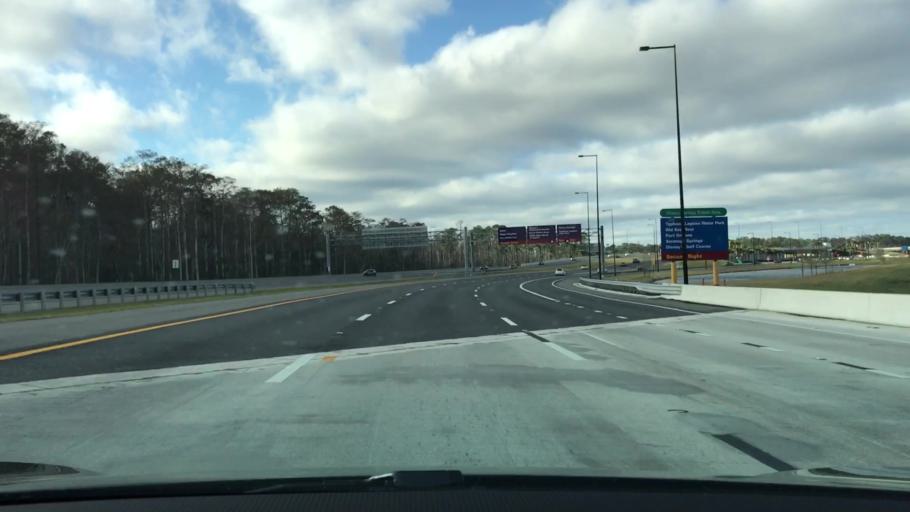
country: US
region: Florida
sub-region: Osceola County
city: Celebration
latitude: 28.3653
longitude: -81.5337
